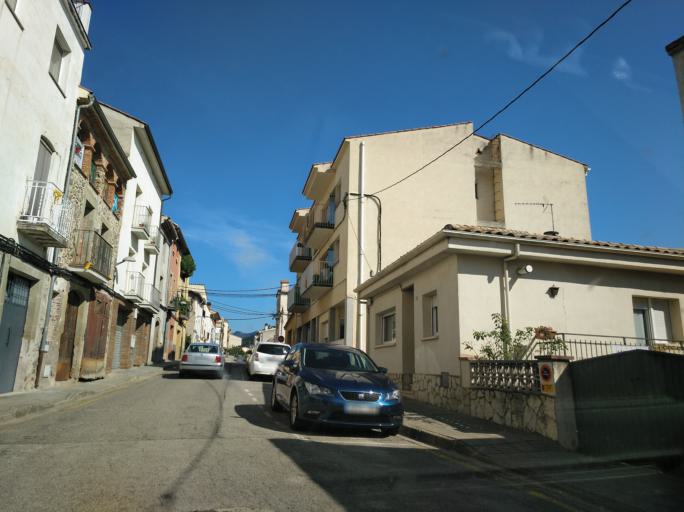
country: ES
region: Catalonia
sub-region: Provincia de Girona
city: la Cellera de Ter
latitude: 42.0098
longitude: 2.6003
